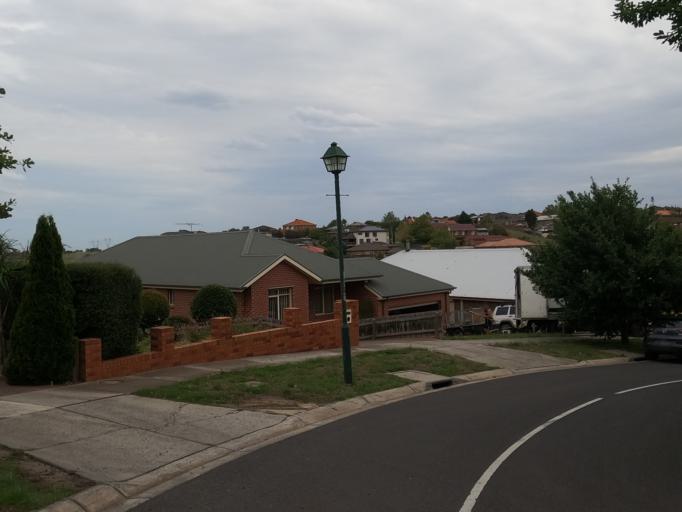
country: AU
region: Victoria
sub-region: Hume
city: Meadow Heights
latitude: -37.6538
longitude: 144.9063
